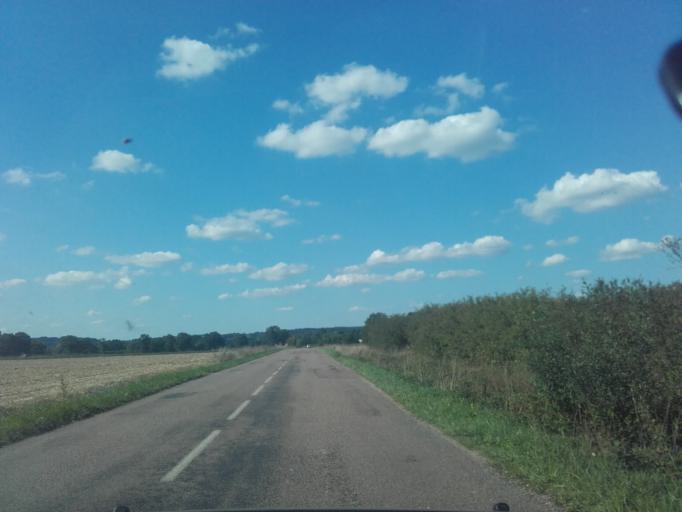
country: FR
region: Bourgogne
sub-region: Departement de Saone-et-Loire
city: Epinac
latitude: 46.9969
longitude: 4.4798
